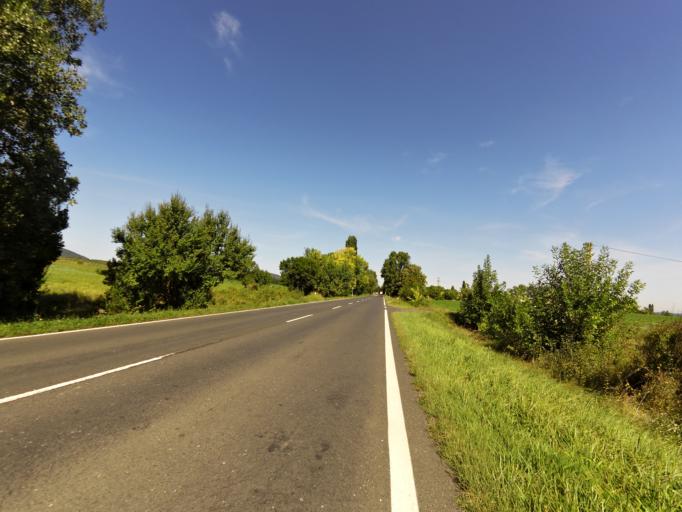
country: HU
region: Veszprem
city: Tapolca
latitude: 46.8305
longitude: 17.3773
